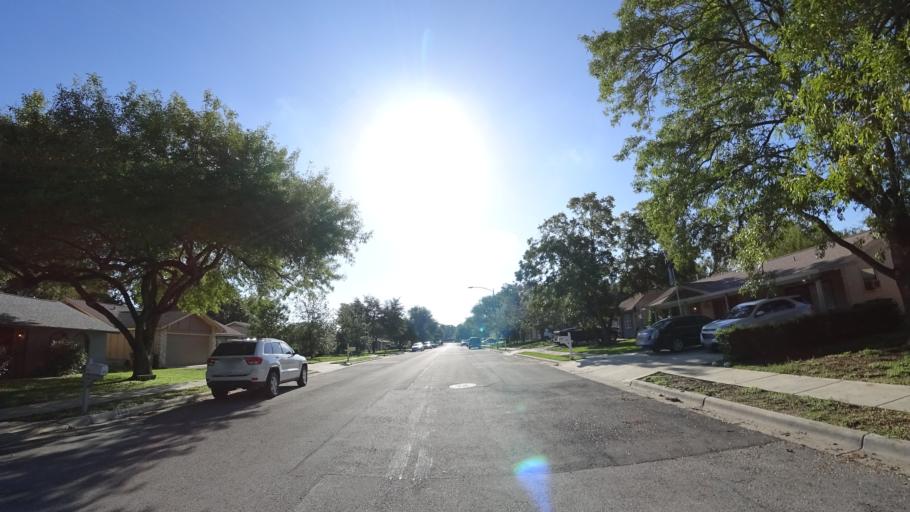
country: US
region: Texas
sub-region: Travis County
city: Rollingwood
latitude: 30.2139
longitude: -97.8122
